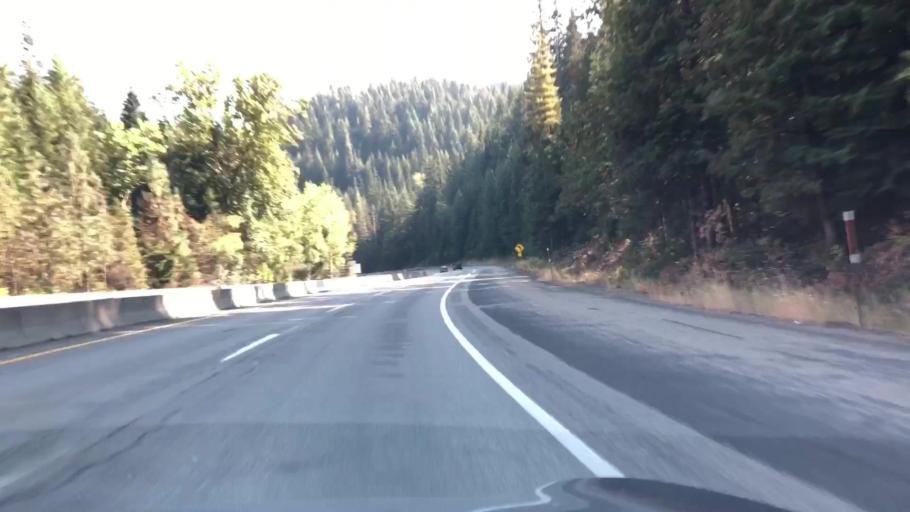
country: US
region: Idaho
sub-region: Kootenai County
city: Coeur d'Alene
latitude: 47.6090
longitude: -116.5123
